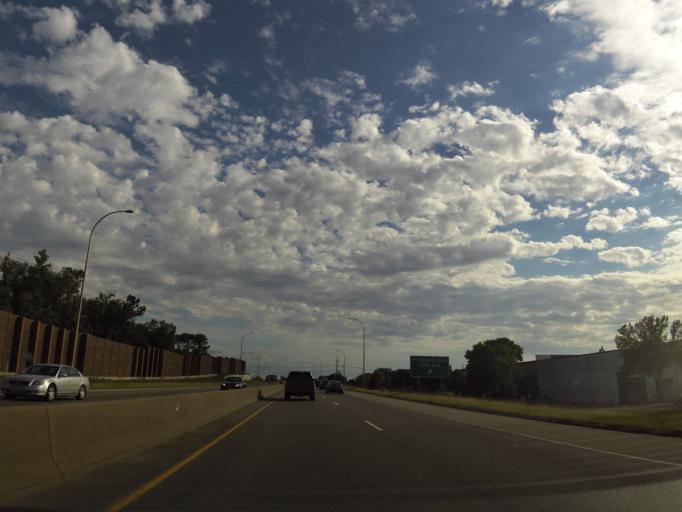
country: US
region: Minnesota
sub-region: Hennepin County
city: New Hope
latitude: 44.9970
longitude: -93.4009
